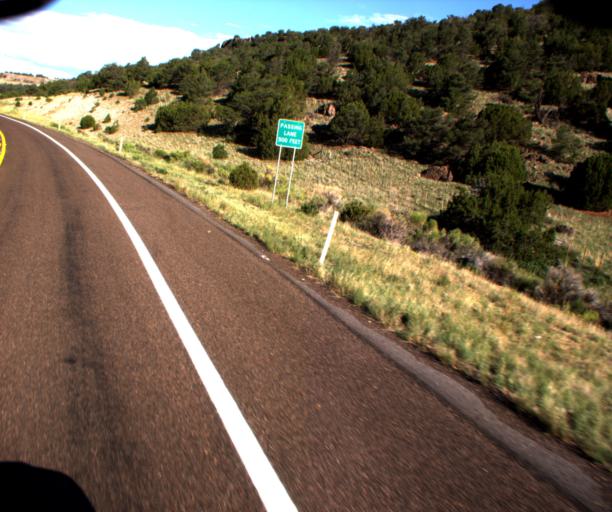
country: US
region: Arizona
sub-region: Apache County
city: Eagar
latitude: 34.0926
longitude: -109.2054
